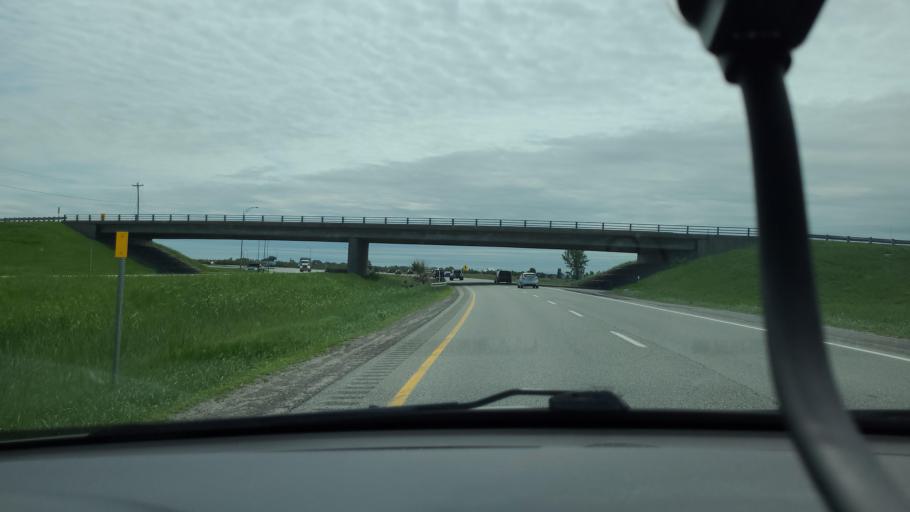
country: CA
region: Quebec
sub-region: Lanaudiere
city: Sainte-Julienne
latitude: 45.8860
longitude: -73.6609
